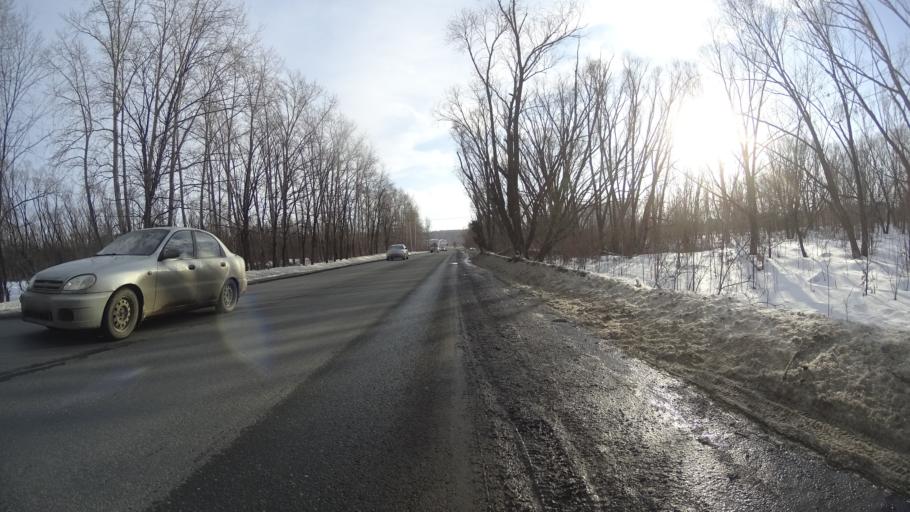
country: RU
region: Chelyabinsk
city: Sargazy
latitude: 55.1427
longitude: 61.2832
